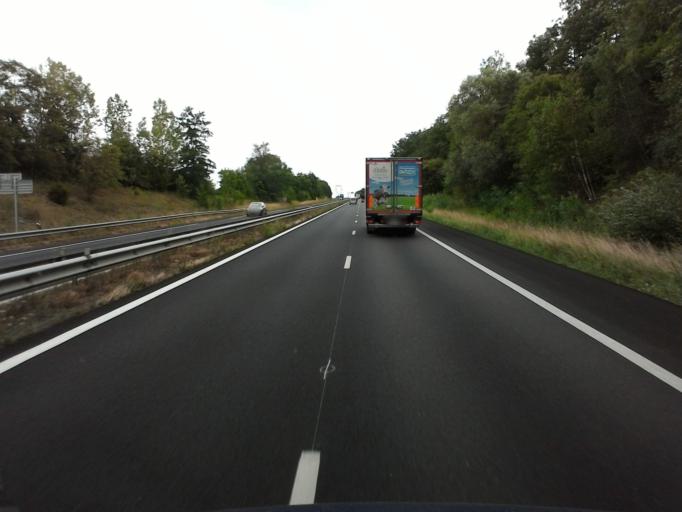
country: FR
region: Lorraine
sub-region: Departement des Vosges
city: Charmes
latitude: 48.4254
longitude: 6.2302
